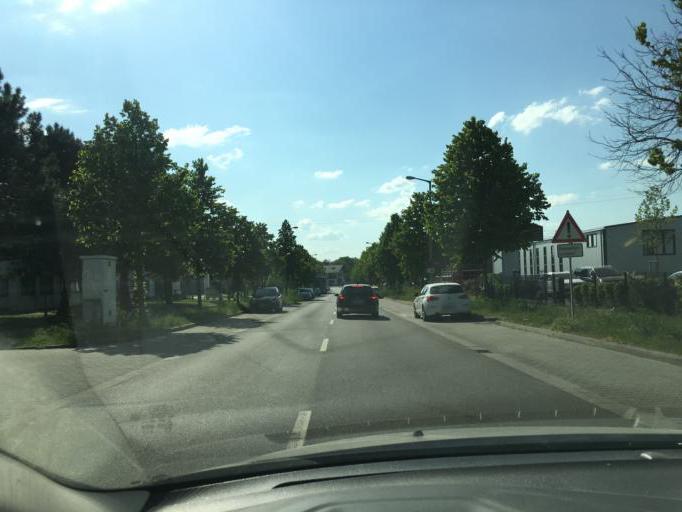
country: DE
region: Saxony
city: Taucha
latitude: 51.3657
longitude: 12.4268
